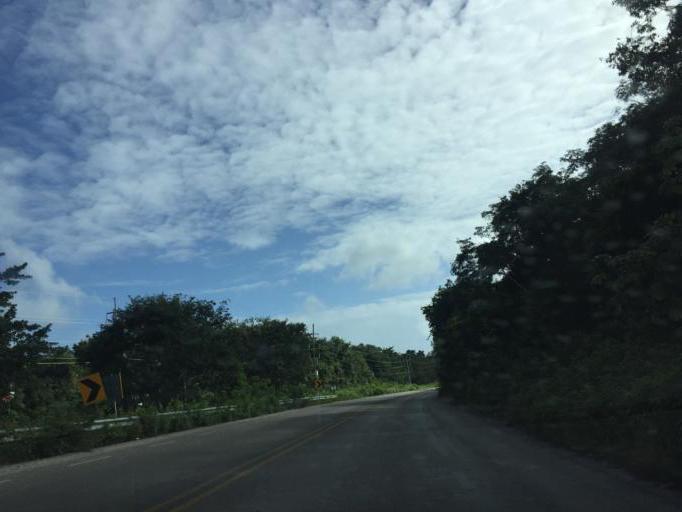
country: MX
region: Quintana Roo
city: Tulum
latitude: 20.2576
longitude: -87.4691
